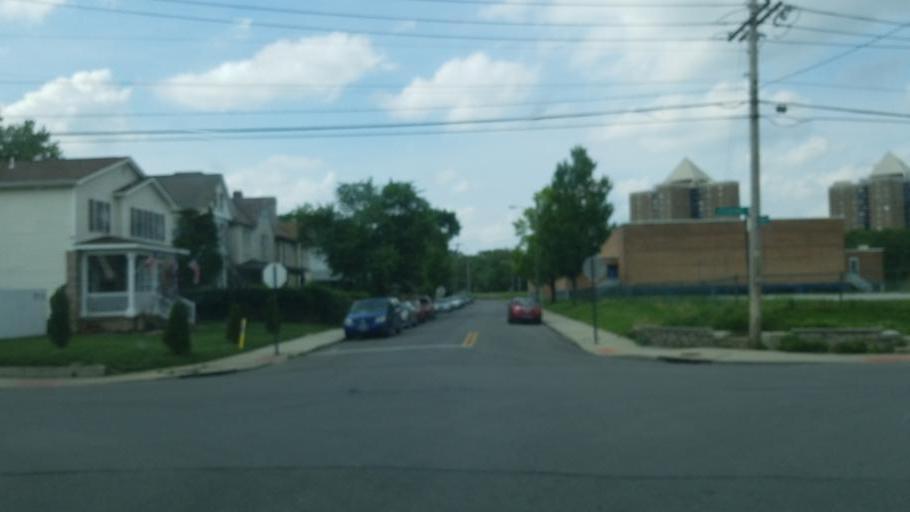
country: US
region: Ohio
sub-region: Franklin County
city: Columbus
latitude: 39.9735
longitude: -82.9782
